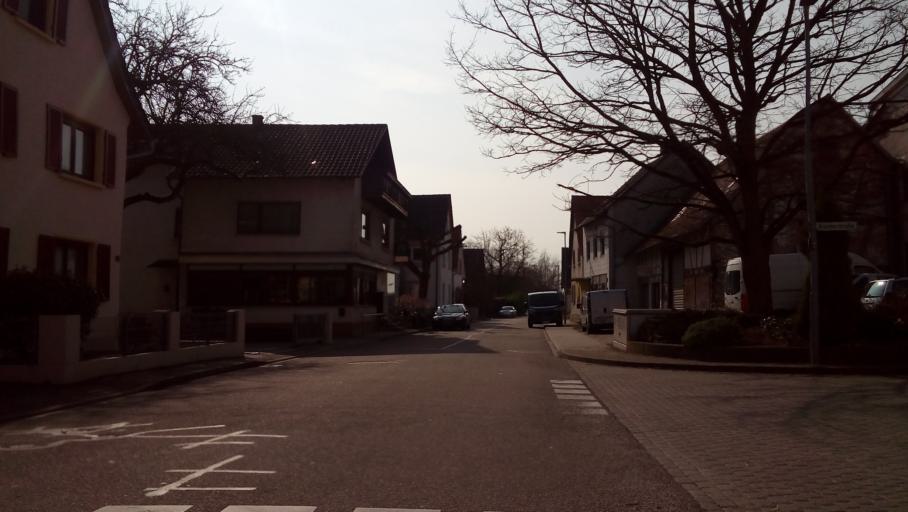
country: DE
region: Baden-Wuerttemberg
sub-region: Freiburg Region
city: Rheinau
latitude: 48.6764
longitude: 7.9403
